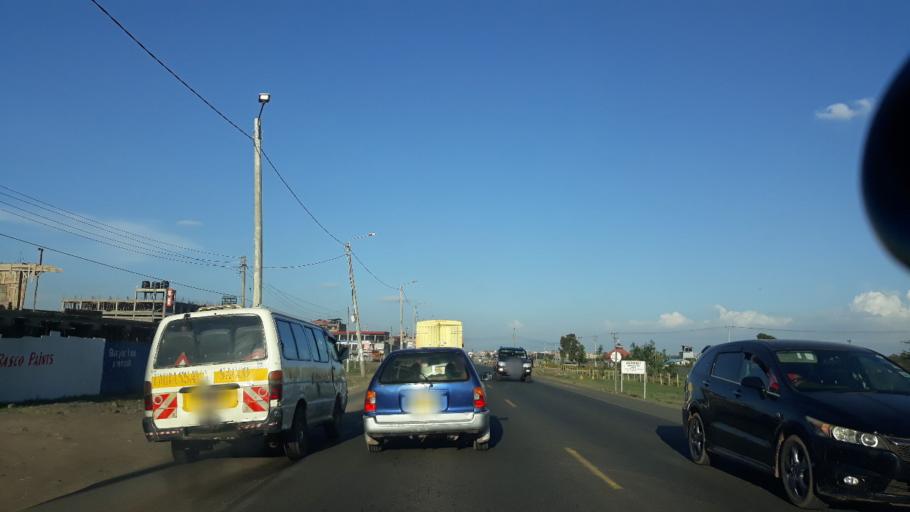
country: KE
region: Nairobi Area
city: Pumwani
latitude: -1.2902
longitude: 36.9482
